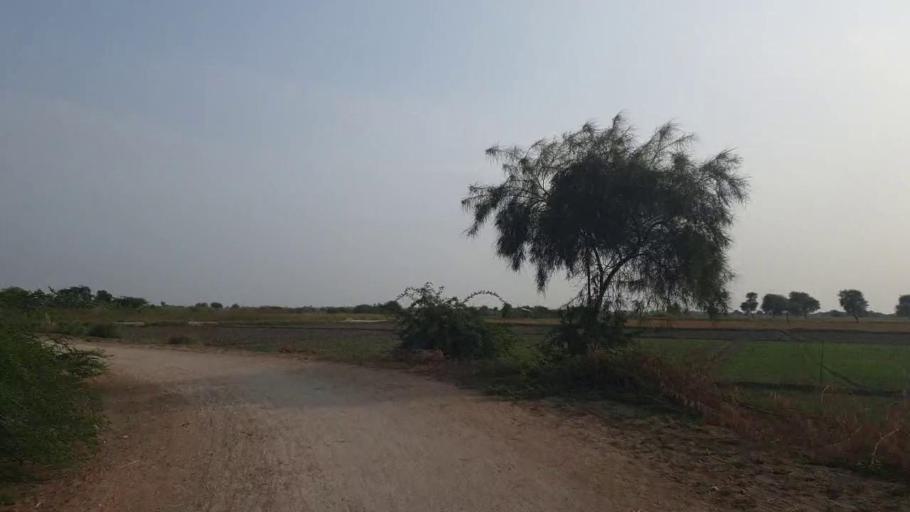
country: PK
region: Sindh
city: Badin
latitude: 24.6070
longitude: 68.6888
